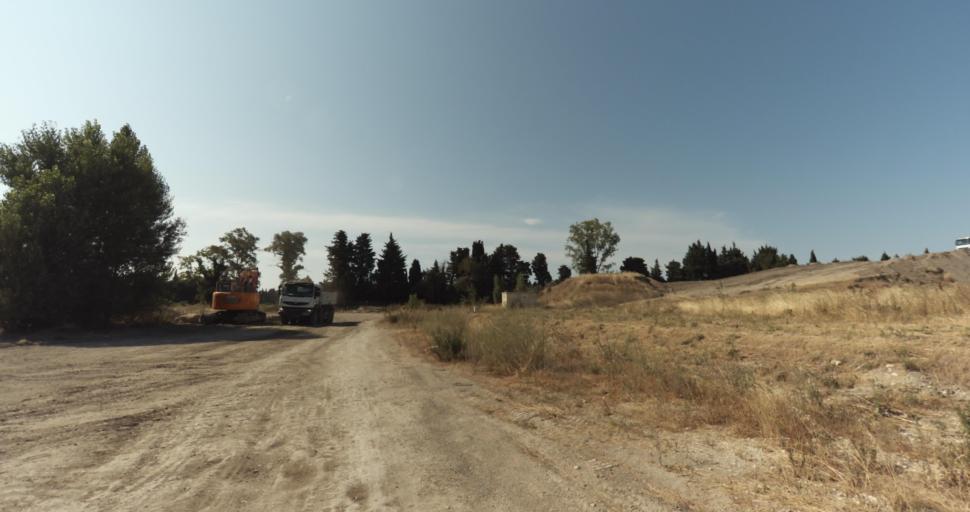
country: FR
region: Provence-Alpes-Cote d'Azur
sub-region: Departement du Vaucluse
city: Althen-des-Paluds
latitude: 44.0146
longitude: 4.9704
